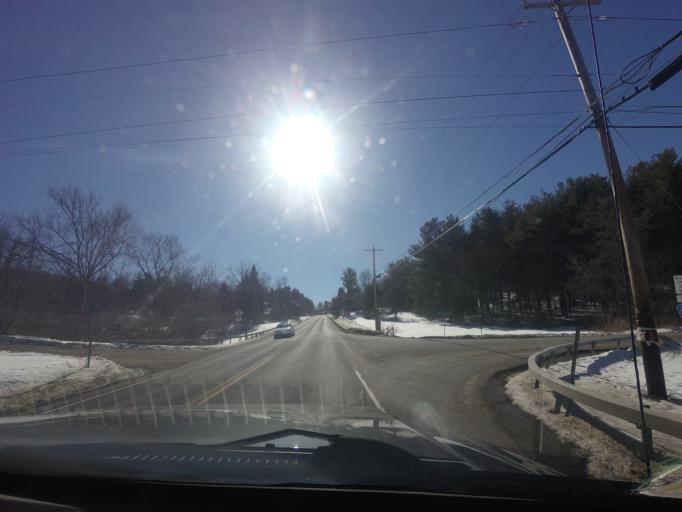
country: US
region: New York
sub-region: Saratoga County
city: Waterford
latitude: 42.8256
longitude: -73.6294
